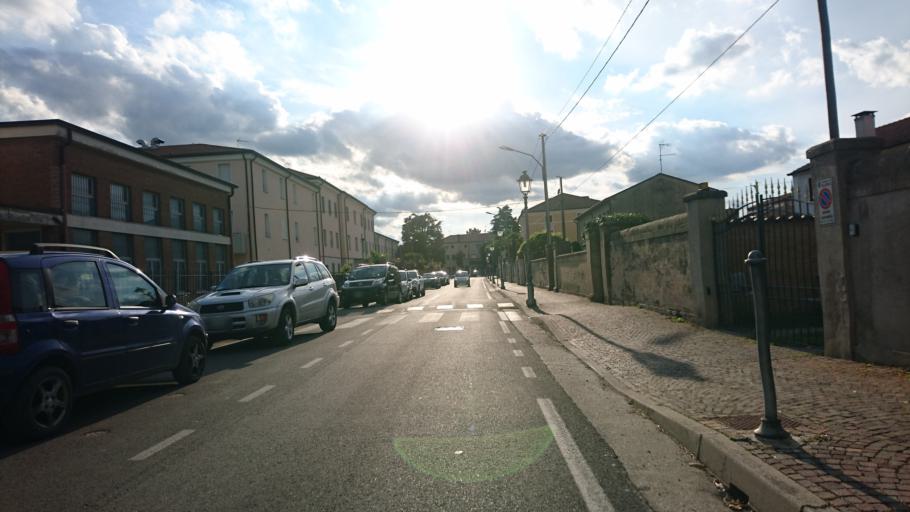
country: IT
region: Veneto
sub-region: Provincia di Rovigo
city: Trecenta
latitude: 45.0292
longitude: 11.4596
